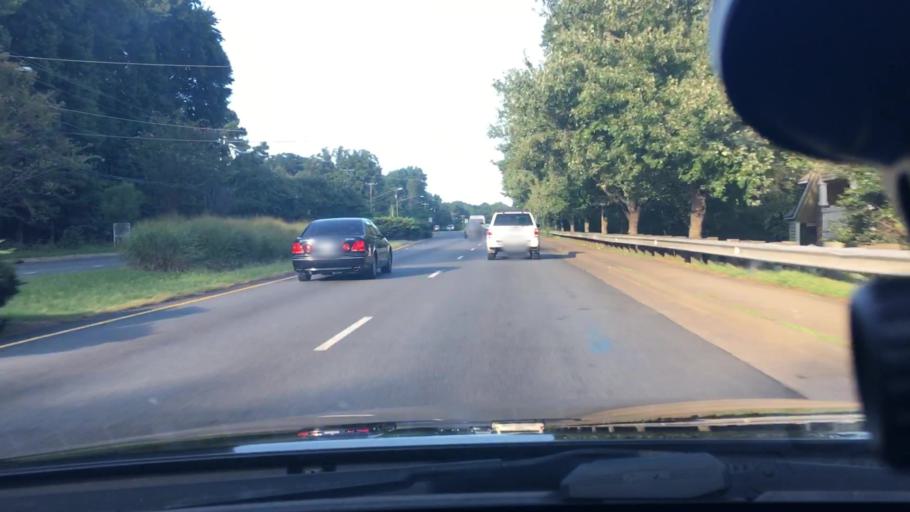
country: US
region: North Carolina
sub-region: Mecklenburg County
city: Mint Hill
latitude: 35.2053
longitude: -80.7170
